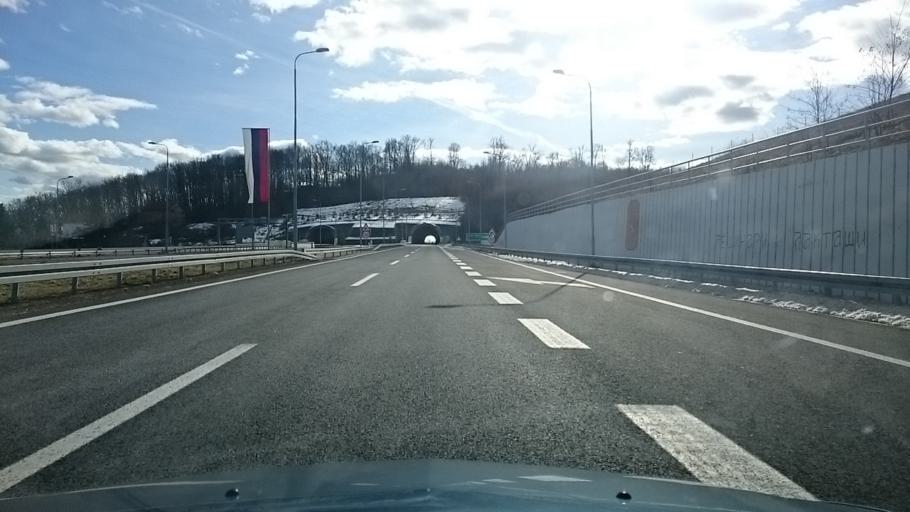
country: BA
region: Republika Srpska
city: Laktasi
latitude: 44.9124
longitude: 17.2961
